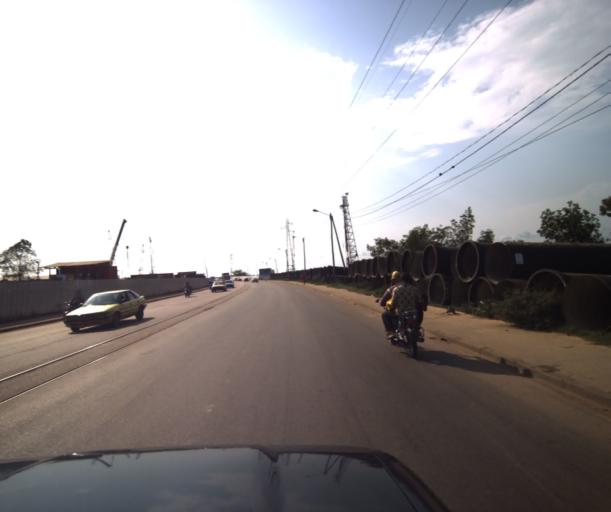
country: CM
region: Littoral
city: Douala
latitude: 4.0716
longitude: 9.6993
